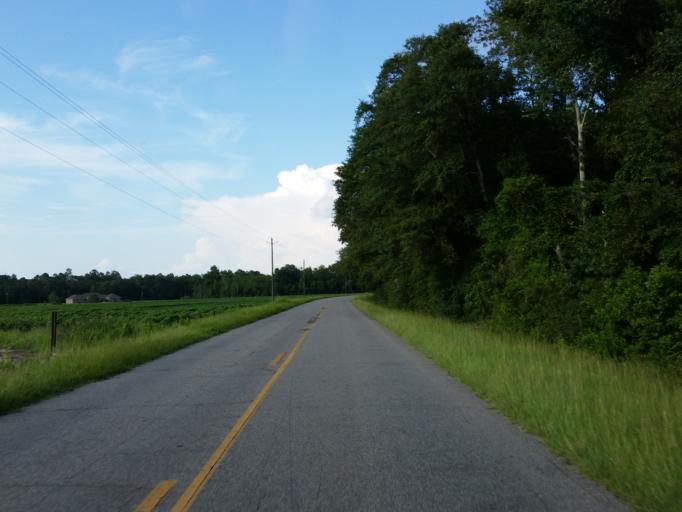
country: US
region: Georgia
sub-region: Dooly County
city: Vienna
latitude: 32.0653
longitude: -83.8213
